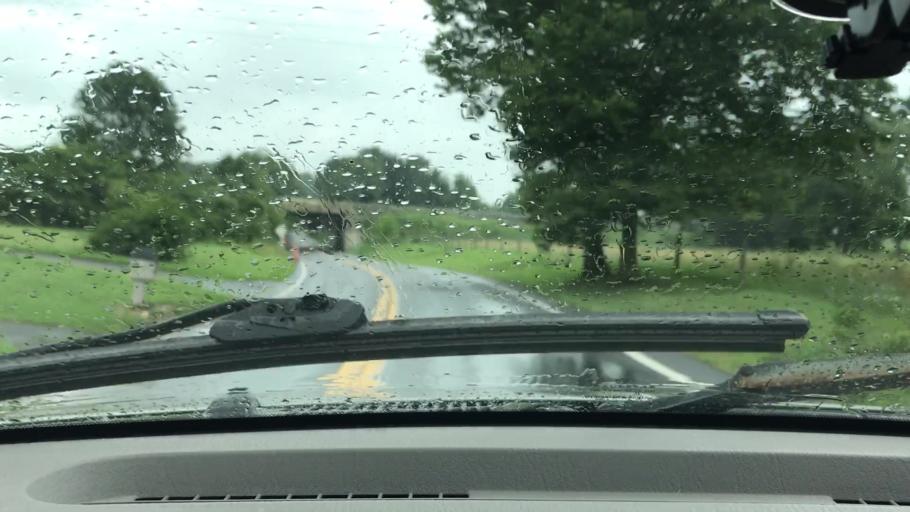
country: US
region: Pennsylvania
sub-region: Lancaster County
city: Elizabethtown
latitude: 40.2068
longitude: -76.6337
